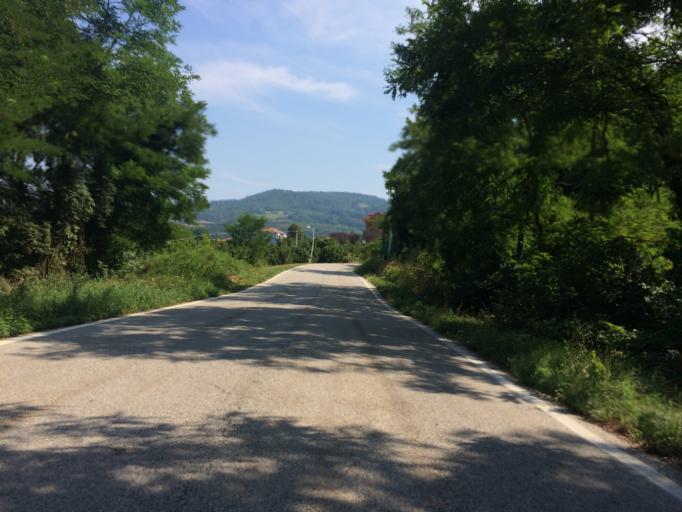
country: IT
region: Piedmont
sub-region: Provincia di Cuneo
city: Torre Bormida
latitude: 44.5668
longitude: 8.1500
